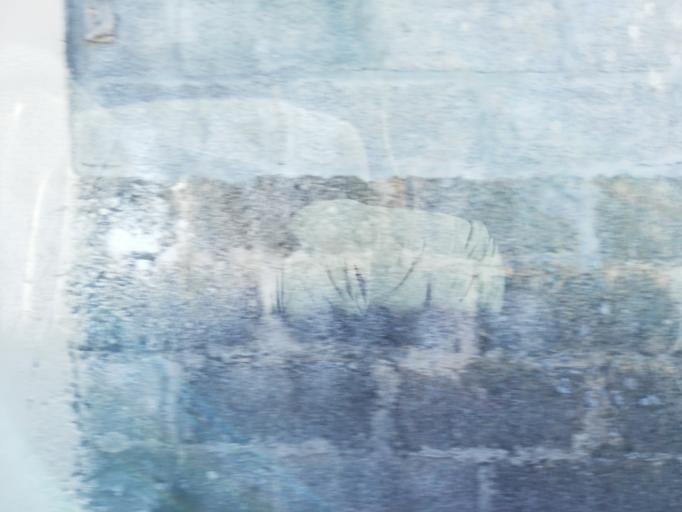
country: MU
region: Port Louis
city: Port Louis
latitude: -20.1642
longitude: 57.4813
